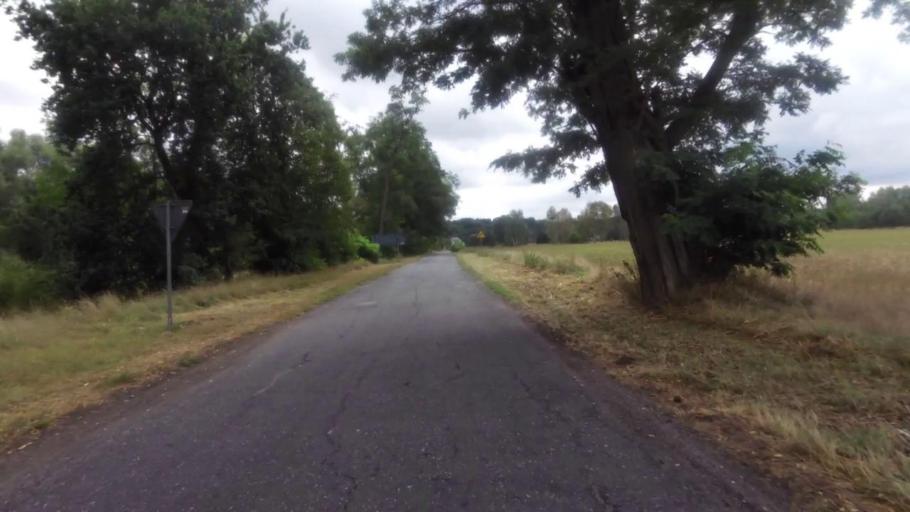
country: PL
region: West Pomeranian Voivodeship
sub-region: Powiat mysliborski
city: Boleszkowice
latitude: 52.6841
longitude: 14.6238
